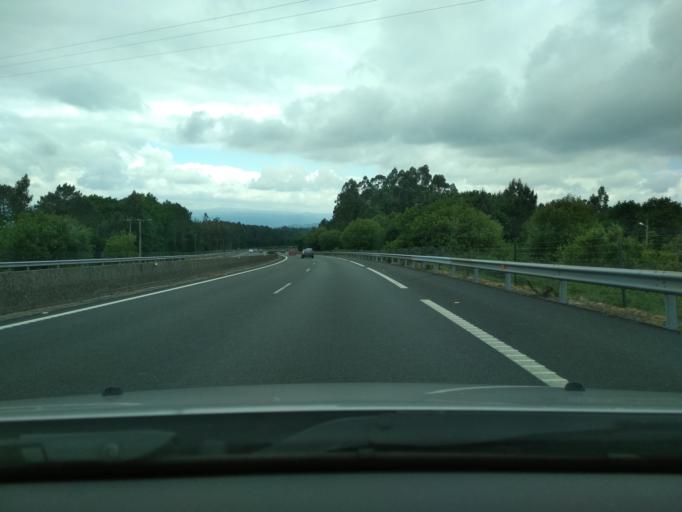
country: ES
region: Galicia
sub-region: Provincia da Coruna
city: Santiago de Compostela
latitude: 42.8272
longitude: -8.5717
